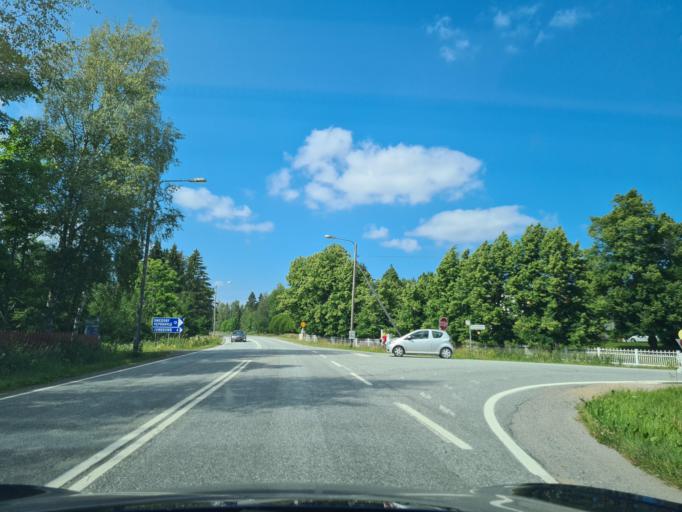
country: FI
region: Ostrobothnia
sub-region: Vaasa
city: Vaasa
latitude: 63.1921
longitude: 21.5614
